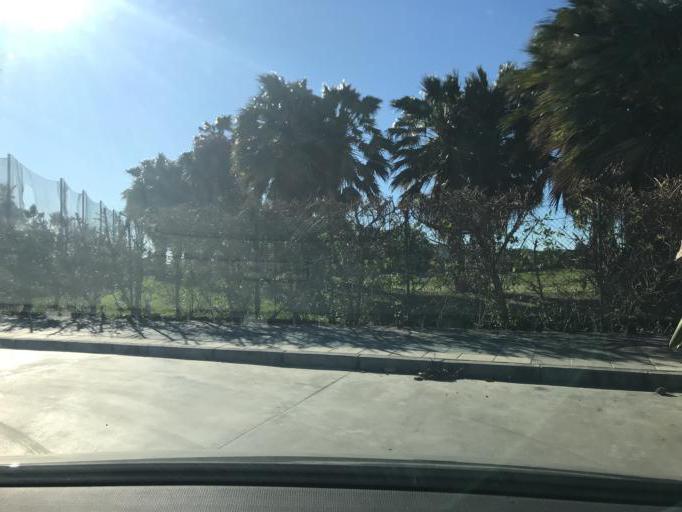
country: ES
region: Andalusia
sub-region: Provincia de Granada
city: Salobrena
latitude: 36.7237
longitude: -3.5642
